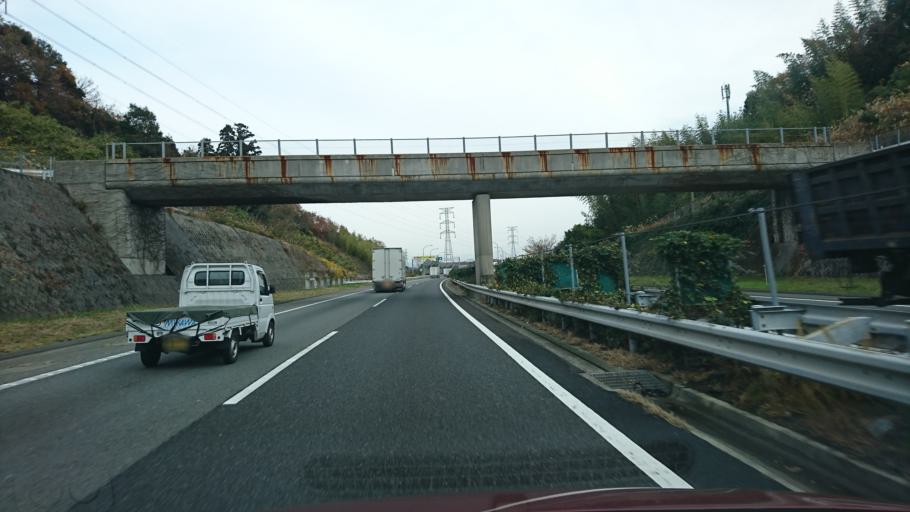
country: JP
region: Hyogo
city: Sandacho
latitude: 34.8275
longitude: 135.1494
